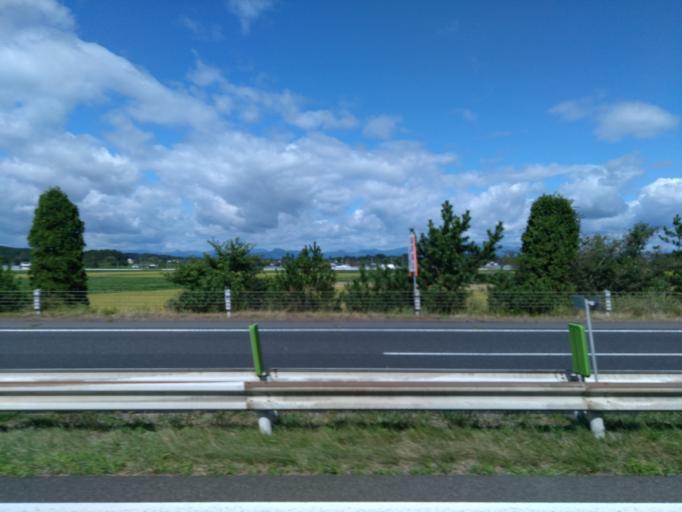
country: JP
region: Iwate
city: Ichinoseki
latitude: 38.7622
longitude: 141.0521
